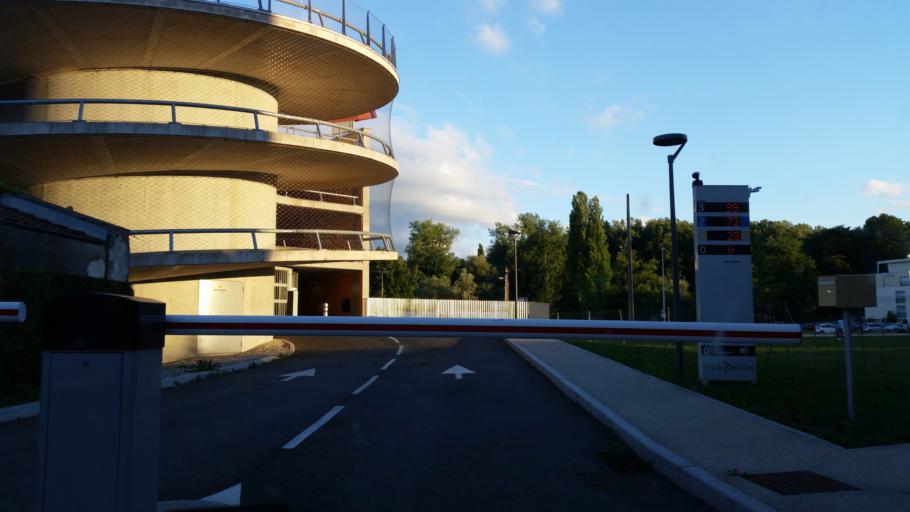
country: FR
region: Franche-Comte
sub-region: Departement du Doubs
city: Montbeliard
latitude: 47.5080
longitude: 6.8015
